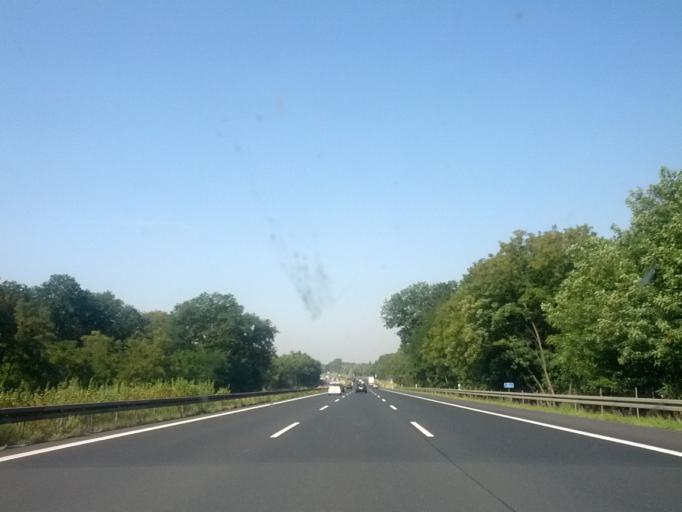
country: DE
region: Brandenburg
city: Rangsdorf
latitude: 52.3073
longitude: 13.3823
